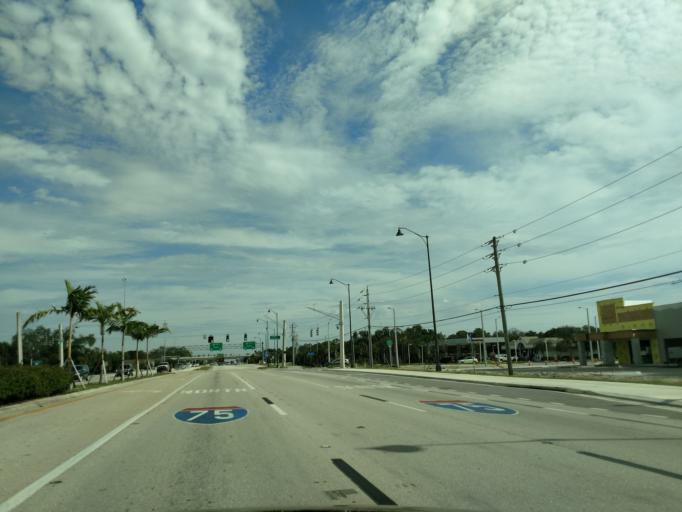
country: US
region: Florida
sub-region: Lee County
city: Bonita Springs
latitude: 26.3313
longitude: -81.7546
